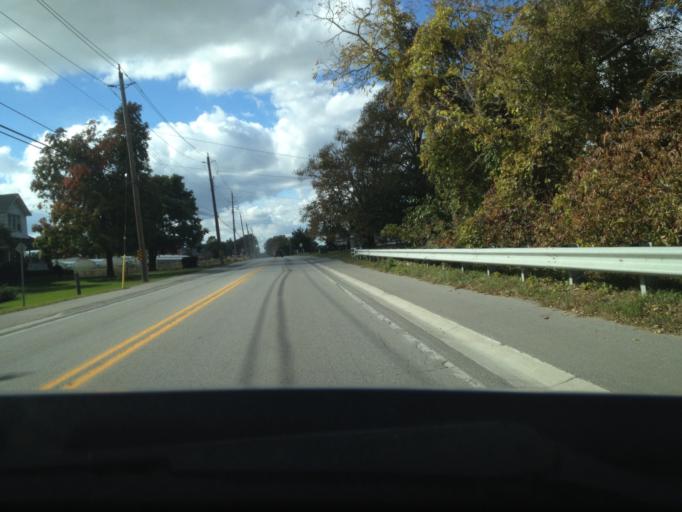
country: CA
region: Ontario
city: Amherstburg
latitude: 42.0397
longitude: -82.6553
